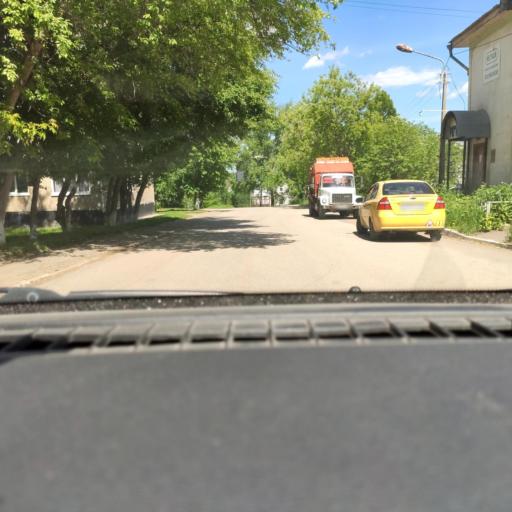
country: RU
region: Perm
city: Chaykovskaya
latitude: 58.1056
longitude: 55.5739
